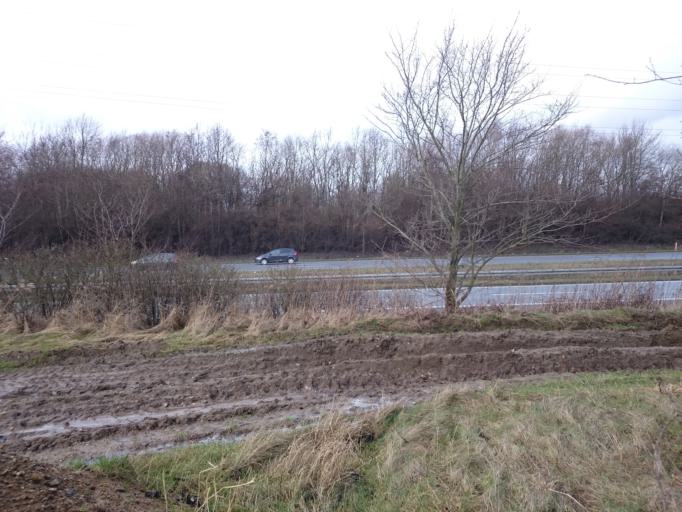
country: DK
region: Central Jutland
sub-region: Arhus Kommune
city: Stavtrup
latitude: 56.1257
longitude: 10.1252
